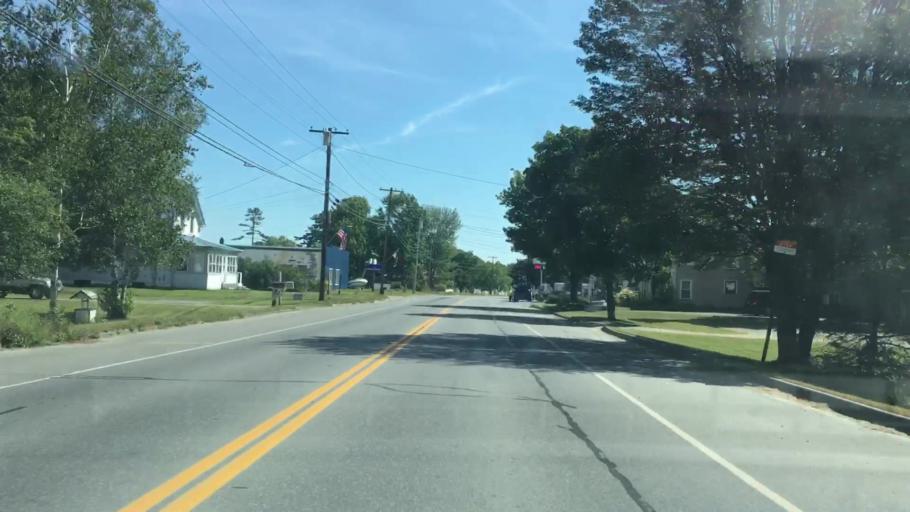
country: US
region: Maine
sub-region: Piscataquis County
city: Milo
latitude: 45.2620
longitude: -68.9896
